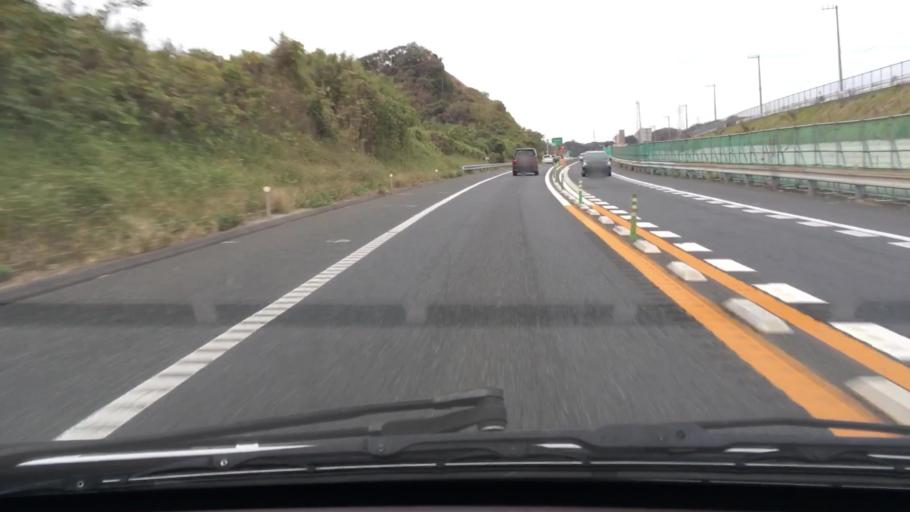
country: JP
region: Chiba
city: Kimitsu
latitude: 35.2420
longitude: 139.8887
